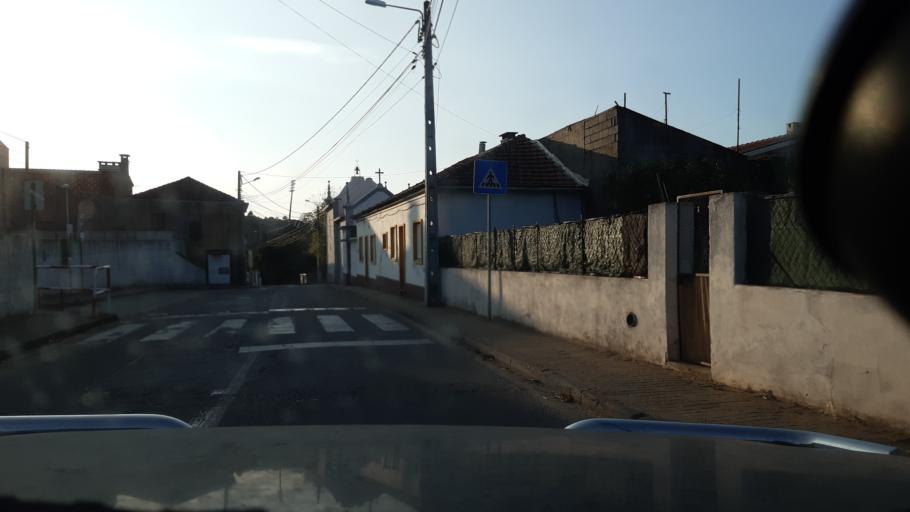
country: PT
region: Aveiro
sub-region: Agueda
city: Agueda
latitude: 40.5604
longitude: -8.4374
